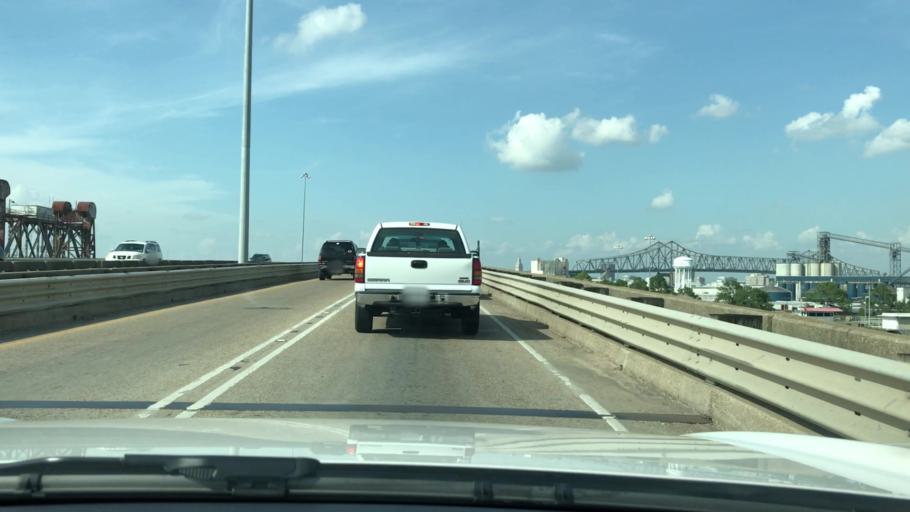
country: US
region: Louisiana
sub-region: West Baton Rouge Parish
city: Port Allen
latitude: 30.4309
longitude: -91.2119
